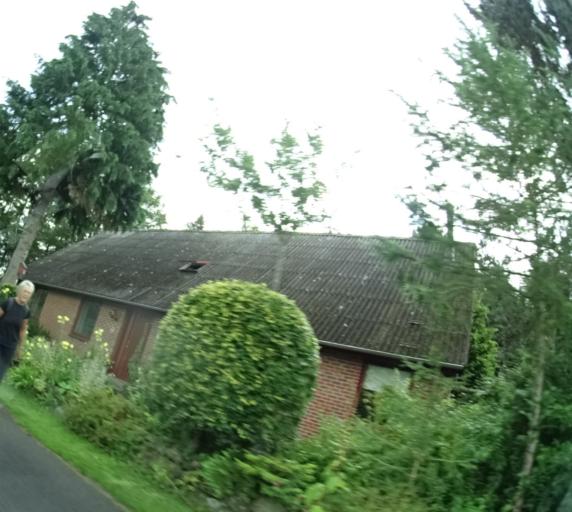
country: DK
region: Central Jutland
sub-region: Syddjurs Kommune
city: Ryomgard
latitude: 56.3973
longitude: 10.4863
